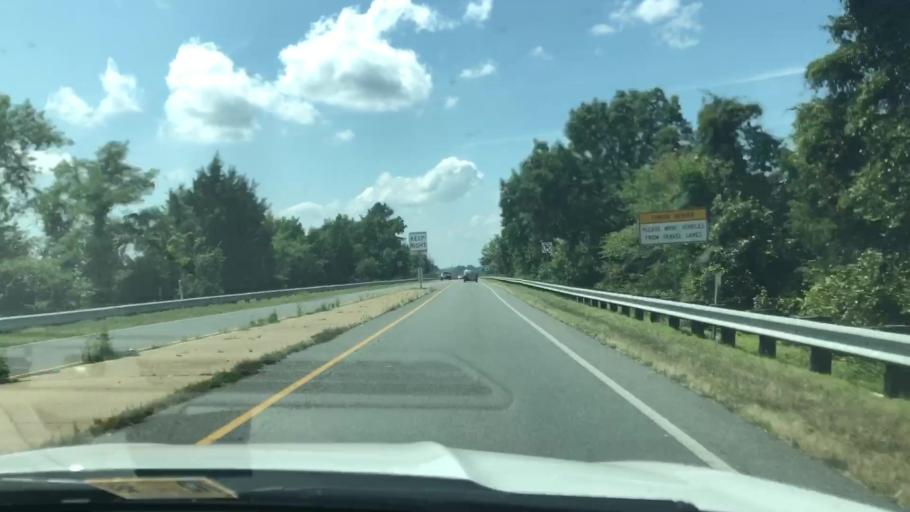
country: US
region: Virginia
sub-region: Essex County
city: Tappahannock
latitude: 37.9427
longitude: -76.8379
